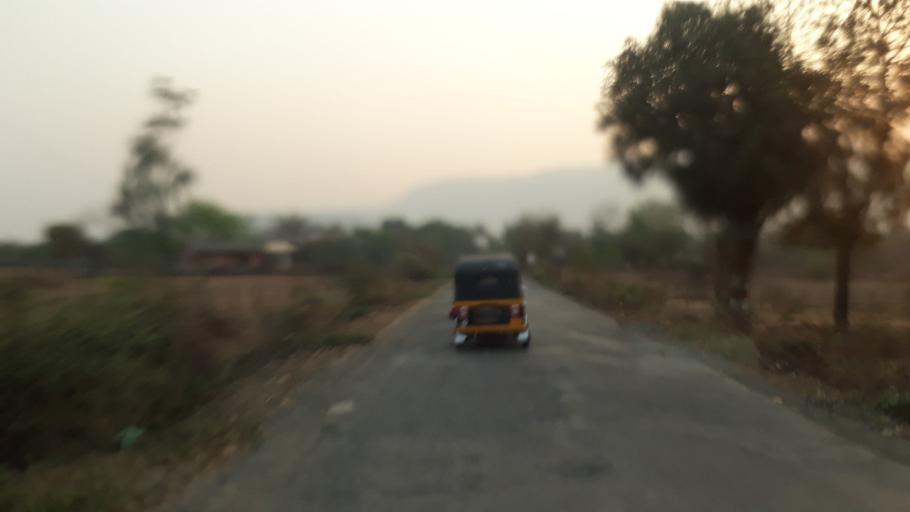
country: IN
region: Maharashtra
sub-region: Raigarh
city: Neral
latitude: 19.0405
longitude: 73.3306
